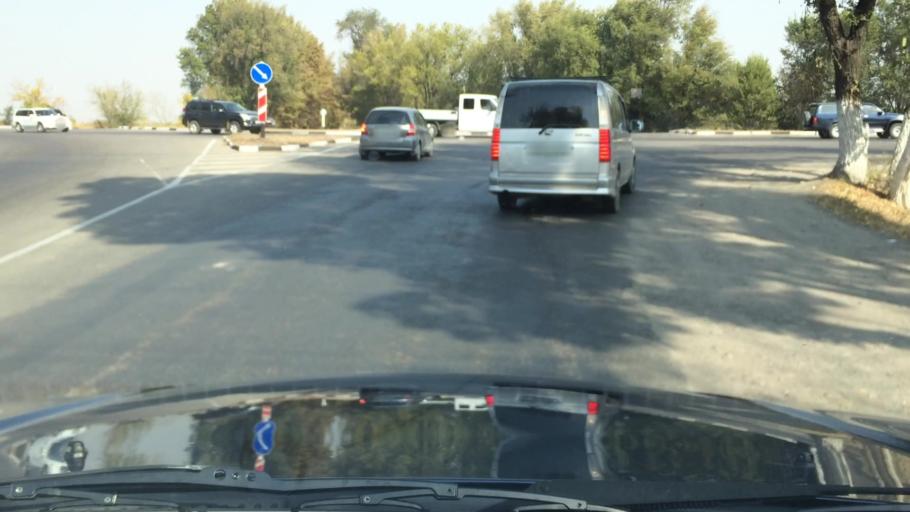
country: KG
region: Chuy
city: Lebedinovka
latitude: 42.9299
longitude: 74.6912
